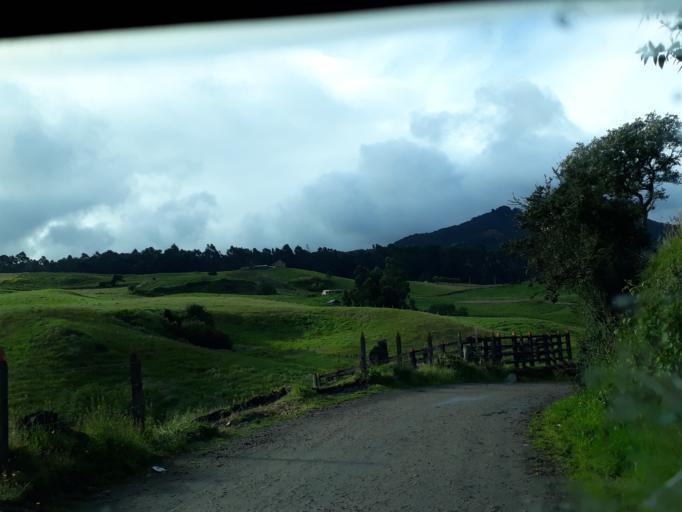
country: CO
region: Cundinamarca
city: Sutatausa
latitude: 5.1875
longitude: -73.8980
